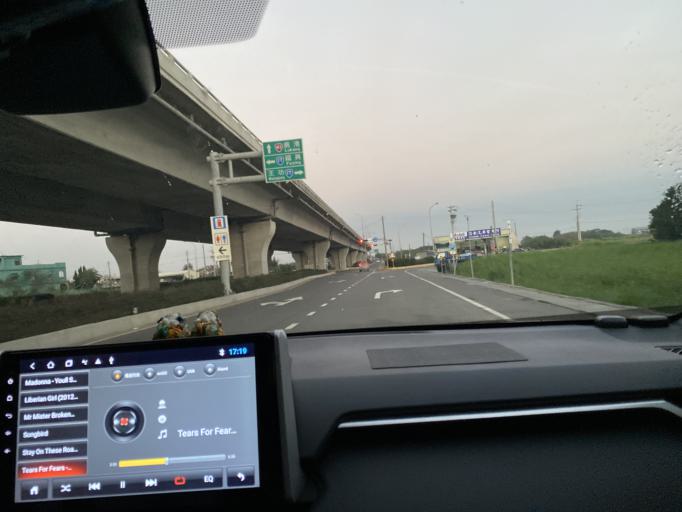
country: TW
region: Taiwan
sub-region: Changhua
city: Chang-hua
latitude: 23.9706
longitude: 120.3485
